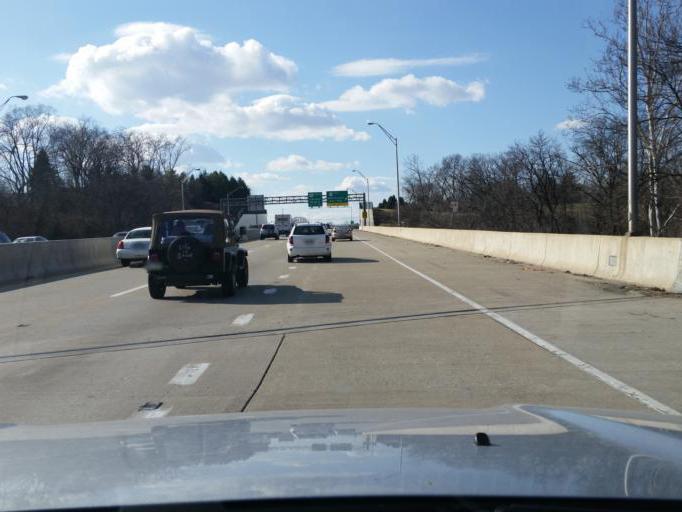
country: US
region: Pennsylvania
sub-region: Lancaster County
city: Lancaster
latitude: 40.0573
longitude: -76.2720
